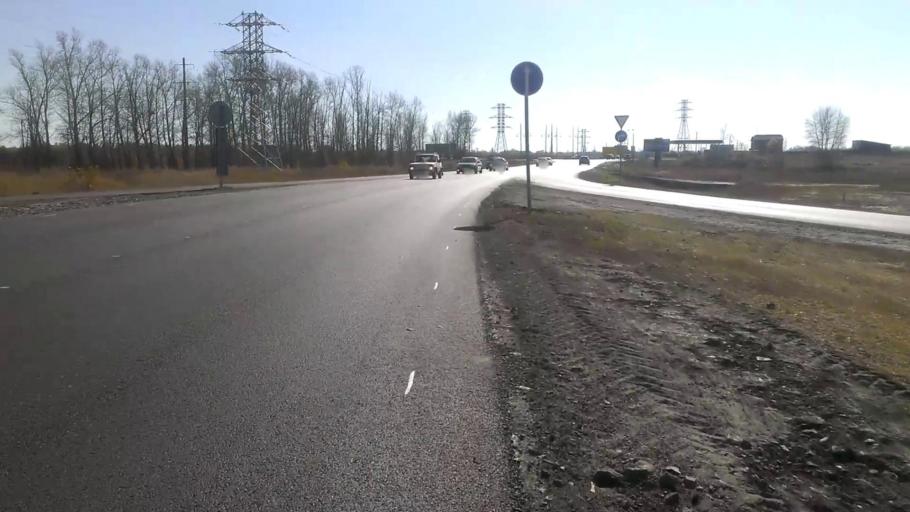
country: RU
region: Altai Krai
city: Sannikovo
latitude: 53.3391
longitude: 83.9384
